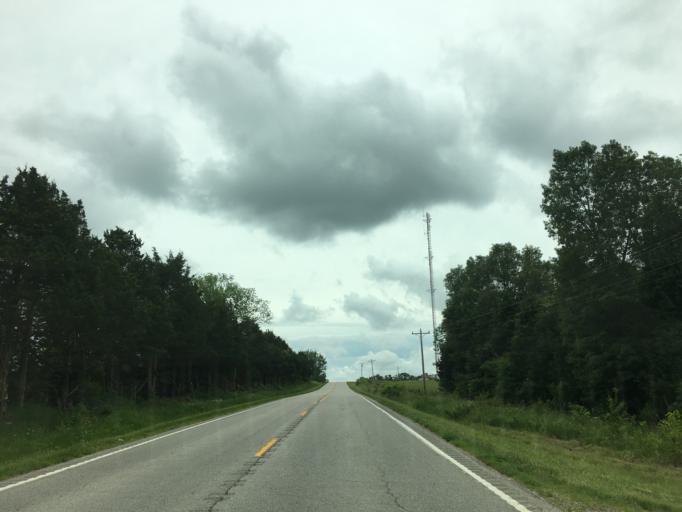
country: US
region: Missouri
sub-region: Gasconade County
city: Owensville
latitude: 38.4925
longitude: -91.4620
